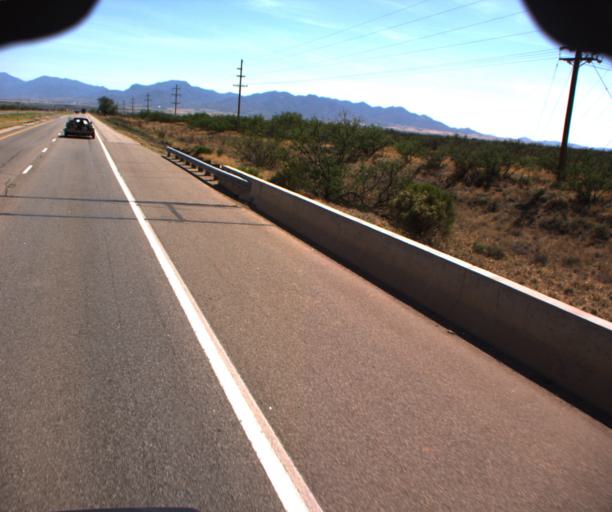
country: US
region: Arizona
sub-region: Cochise County
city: Huachuca City
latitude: 31.6790
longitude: -110.3504
